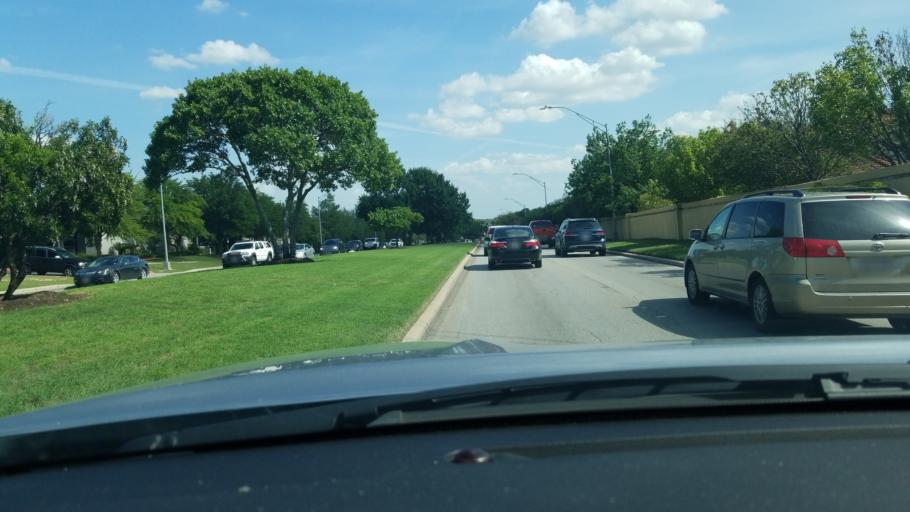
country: US
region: Texas
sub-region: Bexar County
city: Hollywood Park
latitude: 29.6182
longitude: -98.4943
